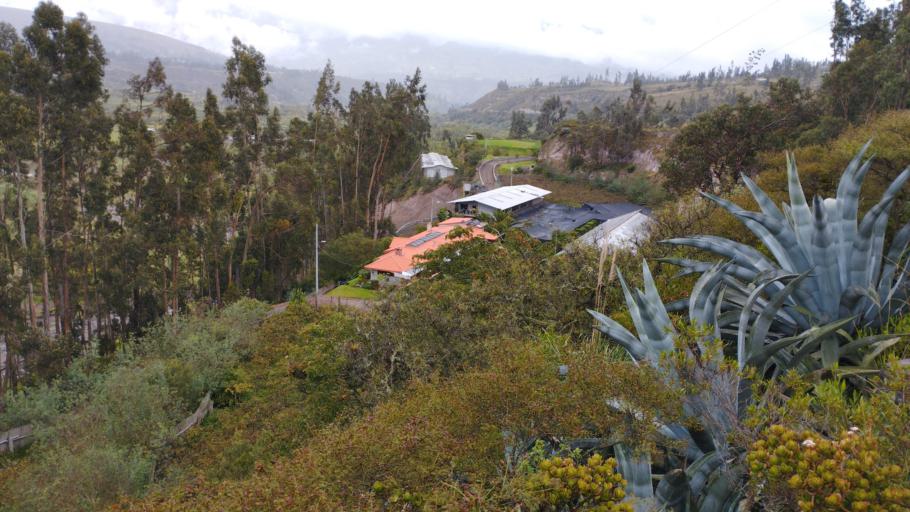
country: EC
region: Chimborazo
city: Guano
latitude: -1.6202
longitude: -78.6102
